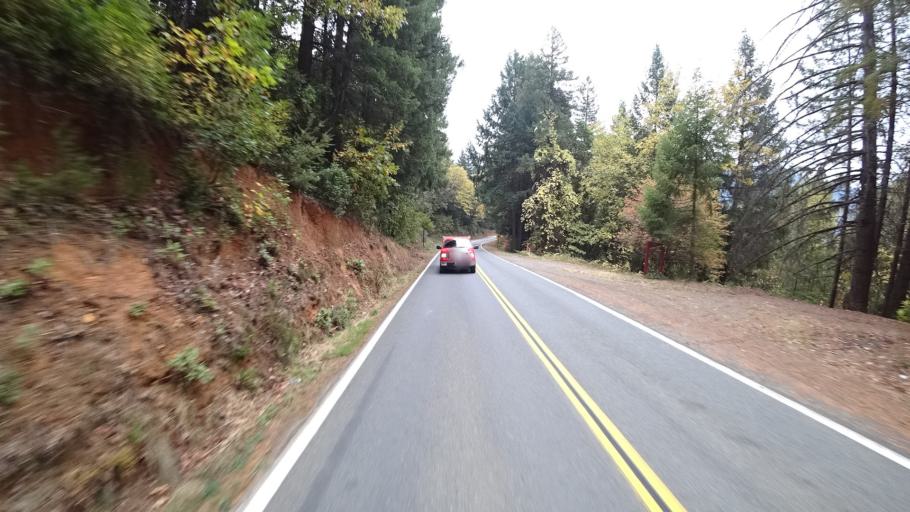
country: US
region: California
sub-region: Siskiyou County
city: Happy Camp
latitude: 41.8095
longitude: -123.3812
